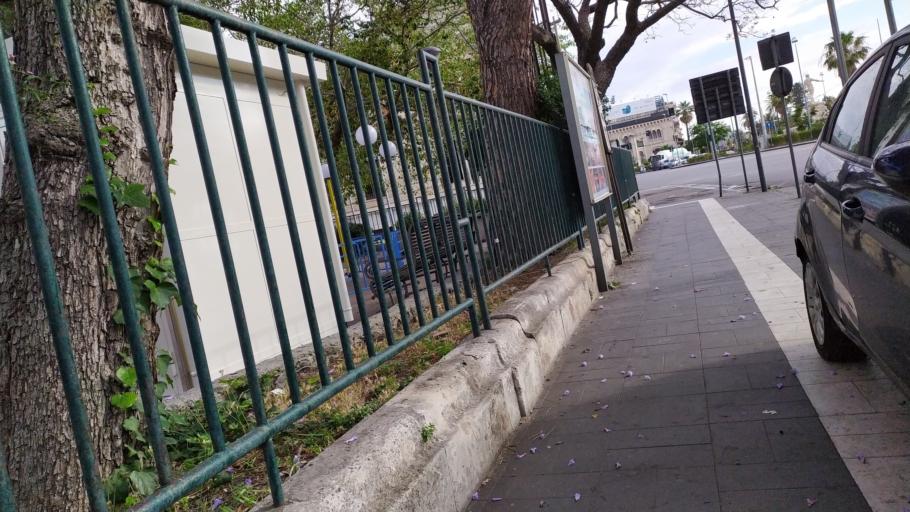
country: IT
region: Sicily
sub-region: Messina
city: Messina
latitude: 38.1987
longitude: 15.5571
